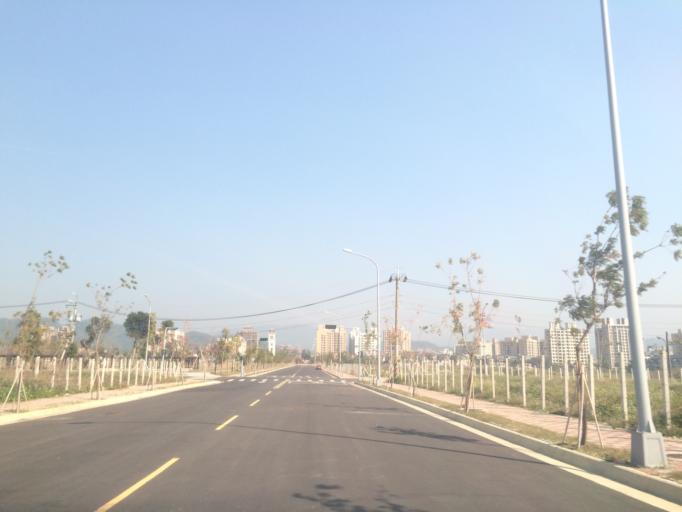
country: TW
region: Taiwan
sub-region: Taichung City
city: Taichung
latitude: 24.1783
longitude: 120.7050
